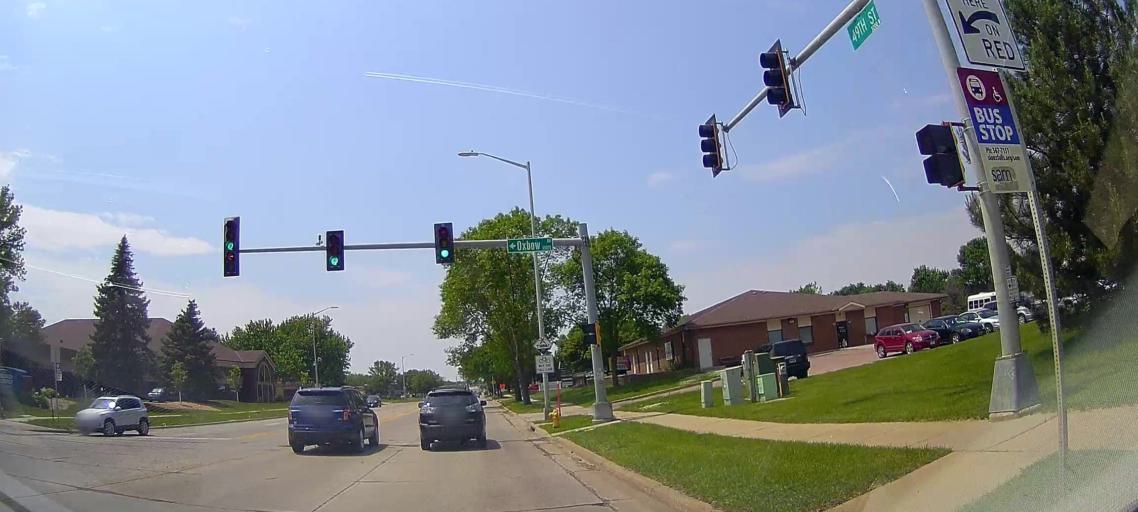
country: US
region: South Dakota
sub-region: Minnehaha County
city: Sioux Falls
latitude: 43.5077
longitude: -96.7659
